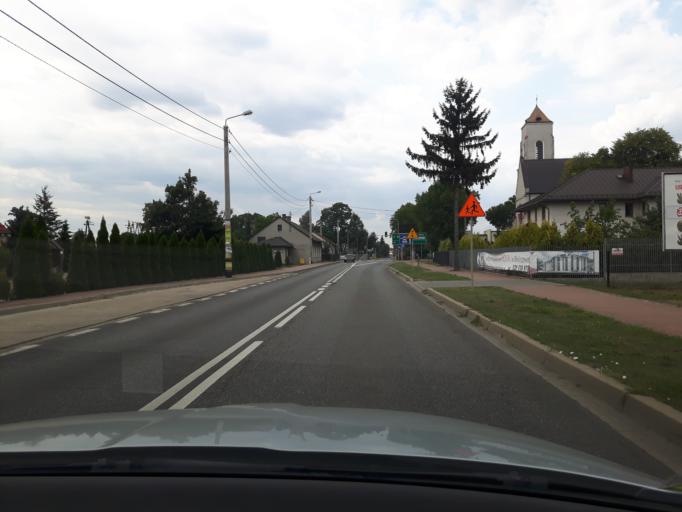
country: PL
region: Masovian Voivodeship
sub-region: Powiat legionowski
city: Wieliszew
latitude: 52.4506
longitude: 20.9711
